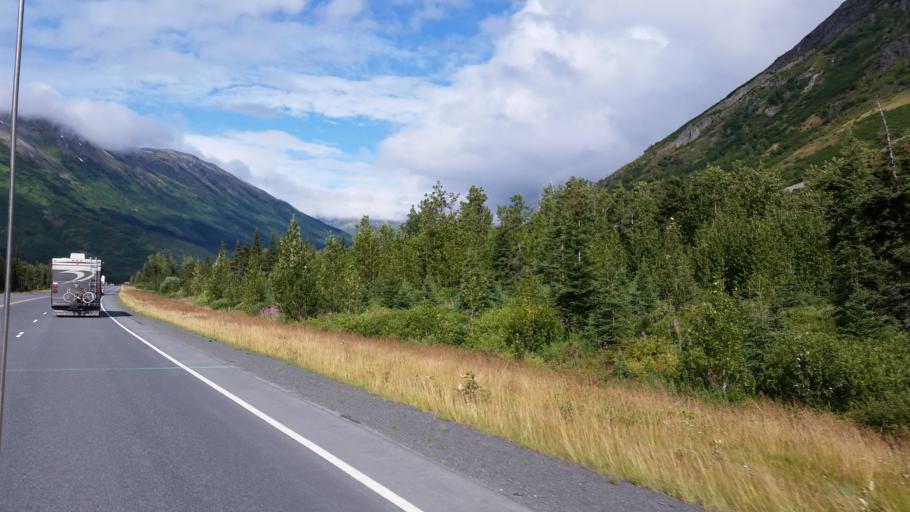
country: US
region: Alaska
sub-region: Anchorage Municipality
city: Girdwood
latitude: 60.7277
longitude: -149.3042
